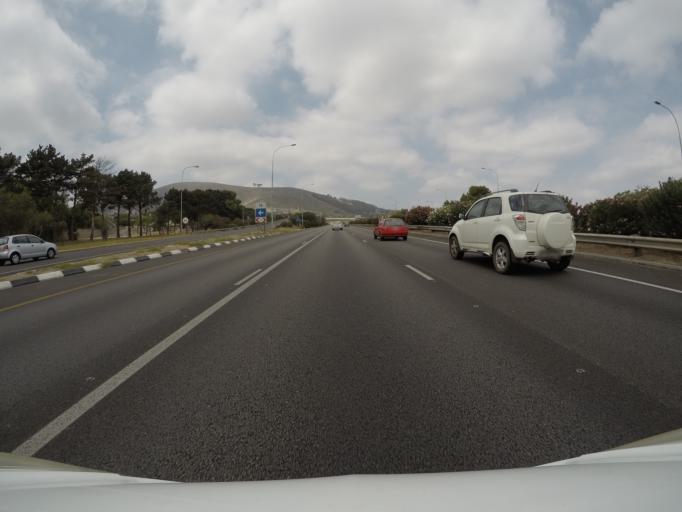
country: ZA
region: Western Cape
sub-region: City of Cape Town
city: Sunset Beach
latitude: -33.8859
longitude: 18.5800
